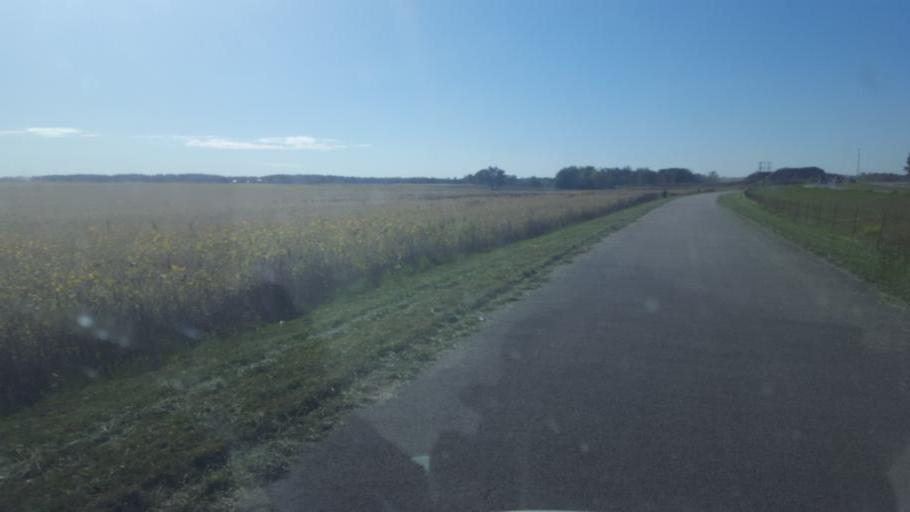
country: US
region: Ohio
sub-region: Wyandot County
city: Upper Sandusky
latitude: 40.8009
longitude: -83.2354
